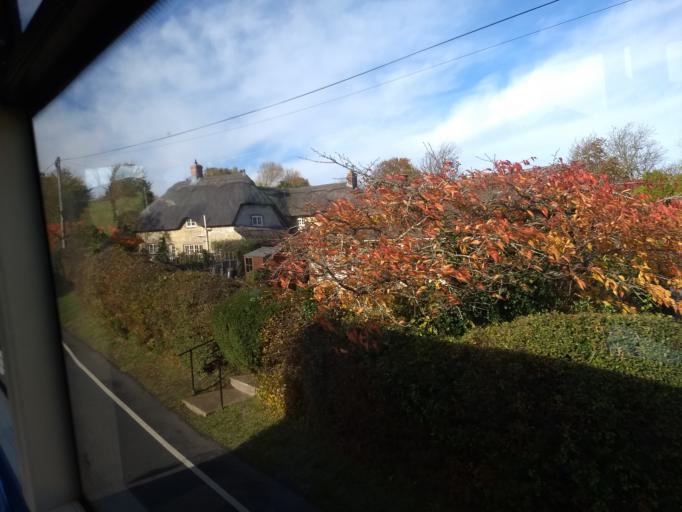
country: GB
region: England
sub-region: Isle of Wight
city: Shalfleet
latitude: 50.6915
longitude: -1.4456
